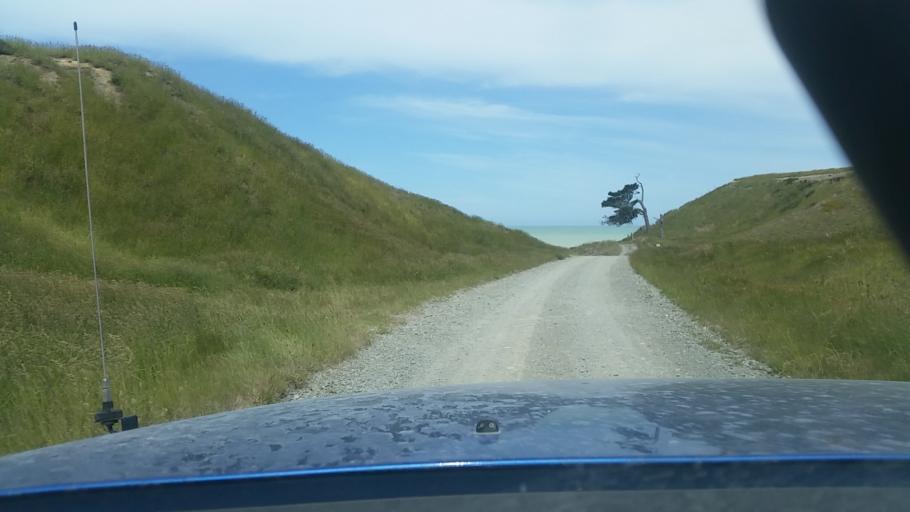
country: NZ
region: Canterbury
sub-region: Ashburton District
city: Tinwald
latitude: -44.0552
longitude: 171.7947
